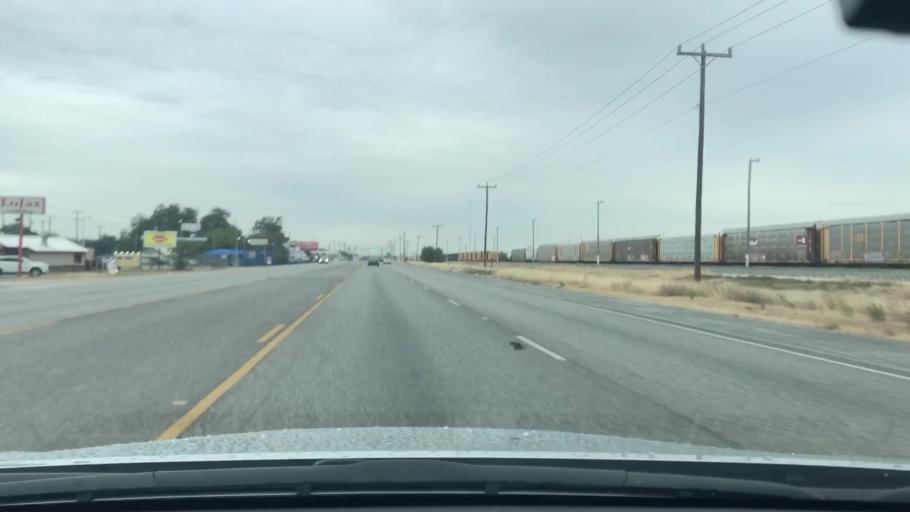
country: US
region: Texas
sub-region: Bexar County
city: Kirby
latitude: 29.4665
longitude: -98.3941
